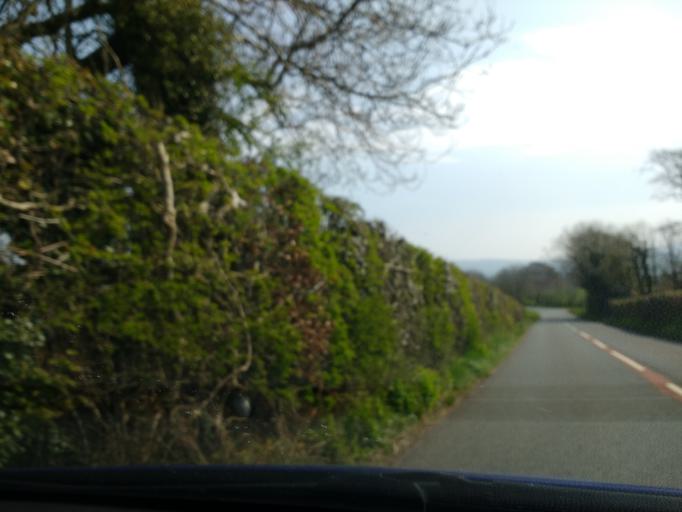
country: GB
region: England
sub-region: Lancashire
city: Bolton le Sands
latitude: 54.0808
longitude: -2.7787
